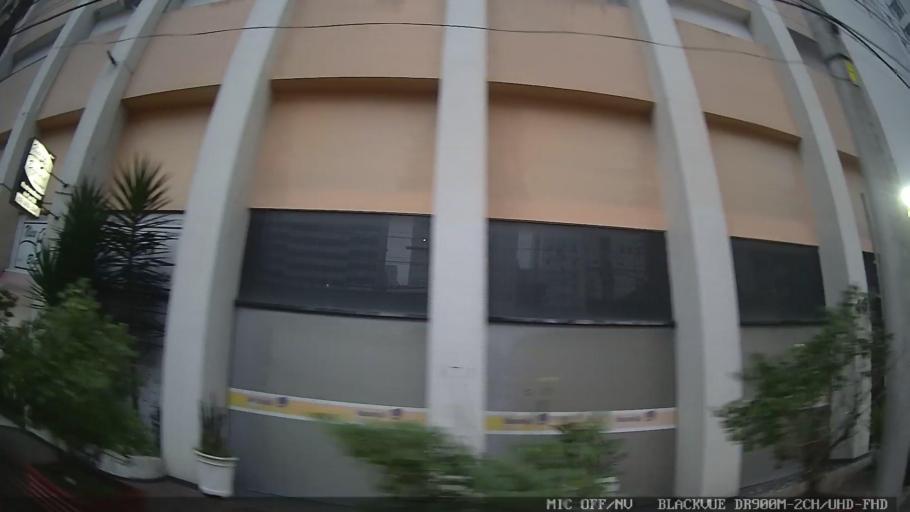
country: BR
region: Sao Paulo
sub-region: Guaruja
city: Guaruja
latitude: -23.9956
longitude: -46.2555
